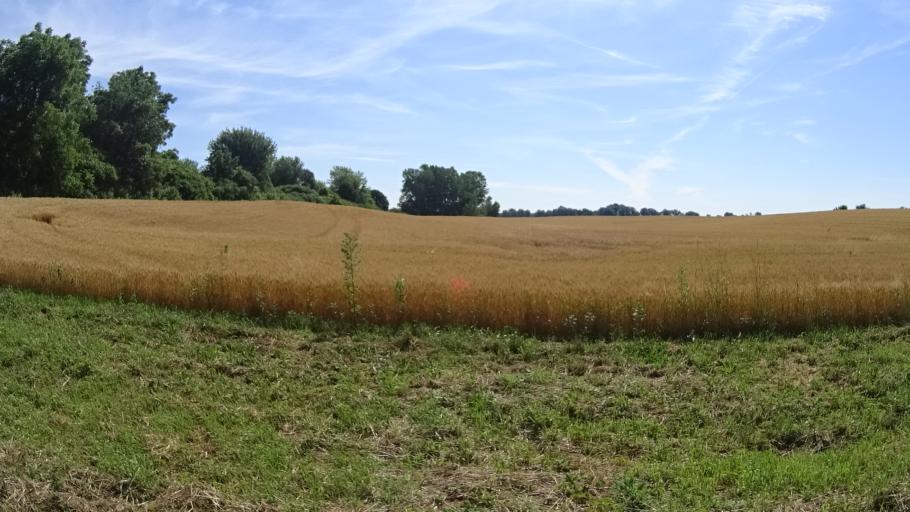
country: US
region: Ohio
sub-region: Erie County
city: Huron
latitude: 41.3782
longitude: -82.4722
